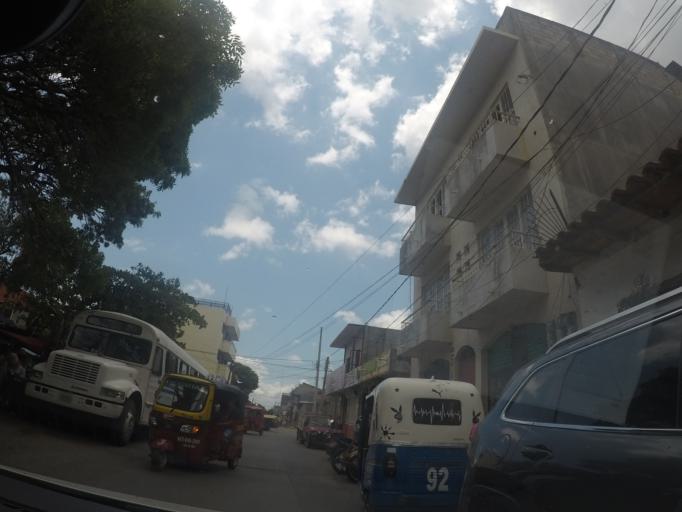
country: MX
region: Oaxaca
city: Juchitan de Zaragoza
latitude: 16.4311
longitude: -95.0231
